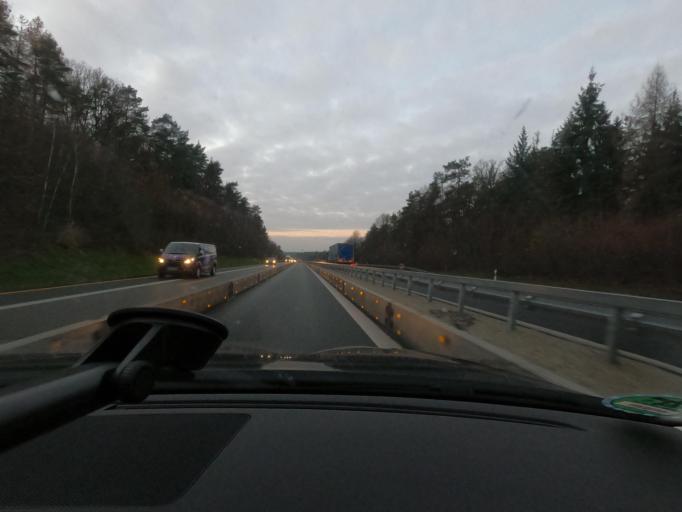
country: DE
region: Bavaria
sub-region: Upper Franconia
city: Strullendorf
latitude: 49.8518
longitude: 10.9864
